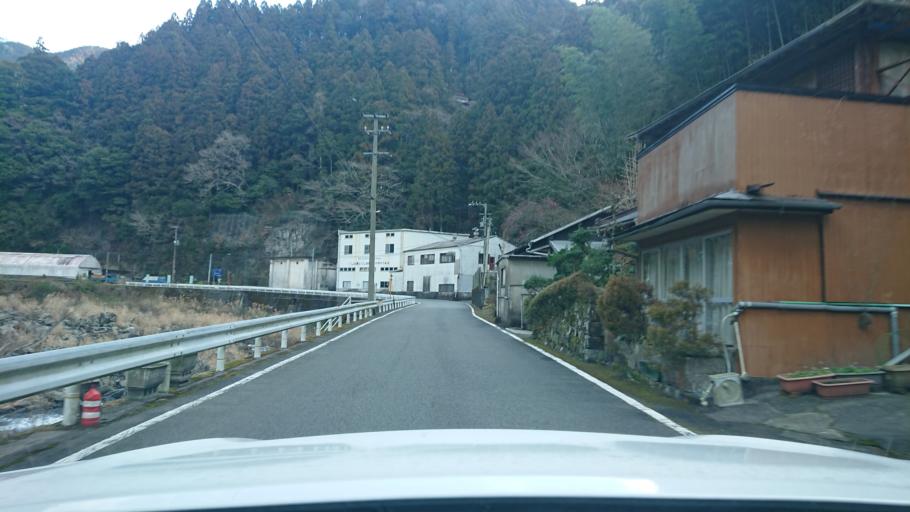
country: JP
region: Tokushima
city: Ishii
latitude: 33.8934
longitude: 134.4027
